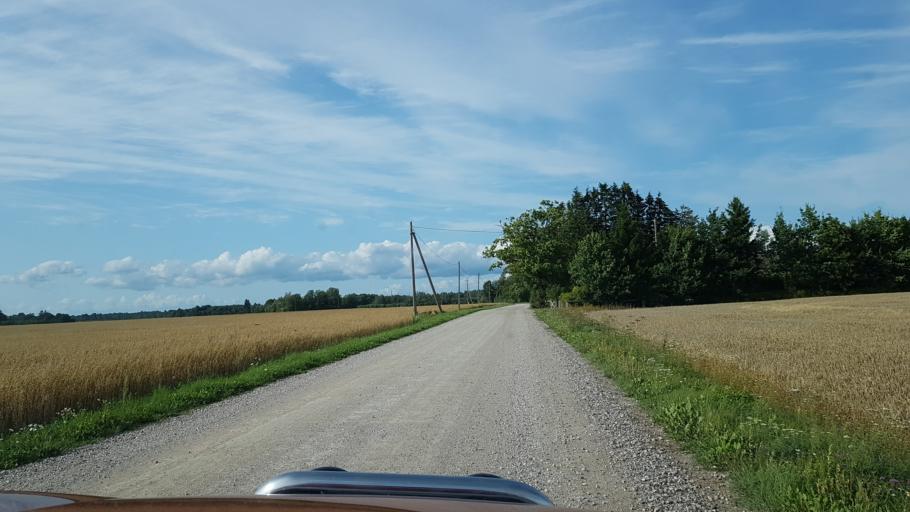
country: EE
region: Laeaene
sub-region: Lihula vald
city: Lihula
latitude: 58.4532
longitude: 23.9962
